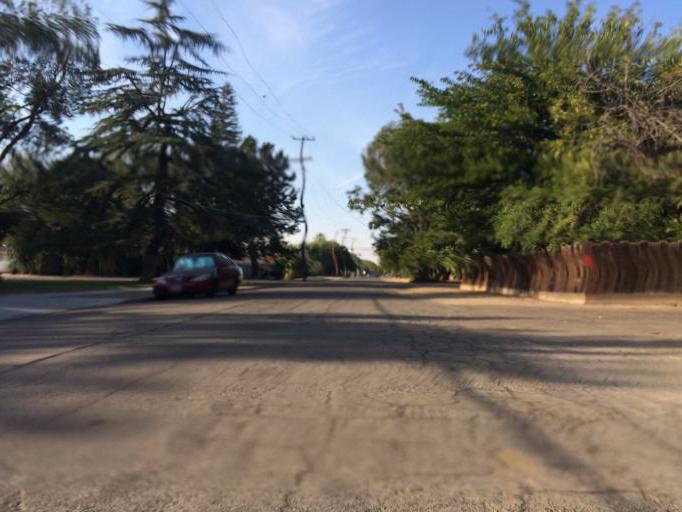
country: US
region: California
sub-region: Fresno County
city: Sunnyside
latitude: 36.7555
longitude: -119.7319
